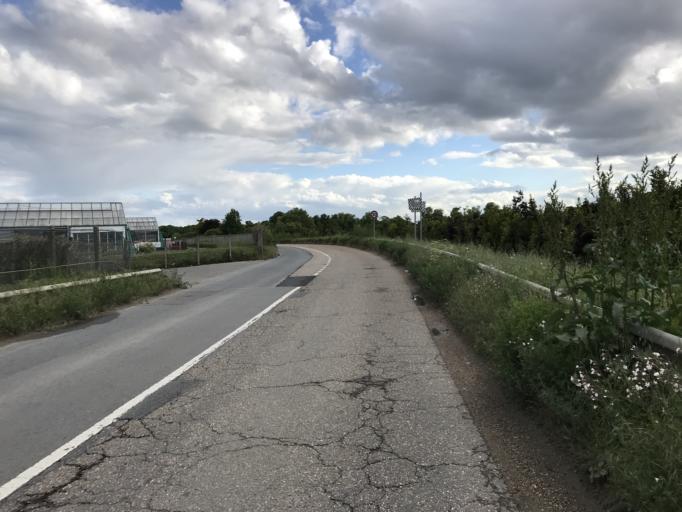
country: FR
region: Ile-de-France
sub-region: Departement du Val-de-Marne
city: Rungis
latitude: 48.7485
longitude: 2.3375
